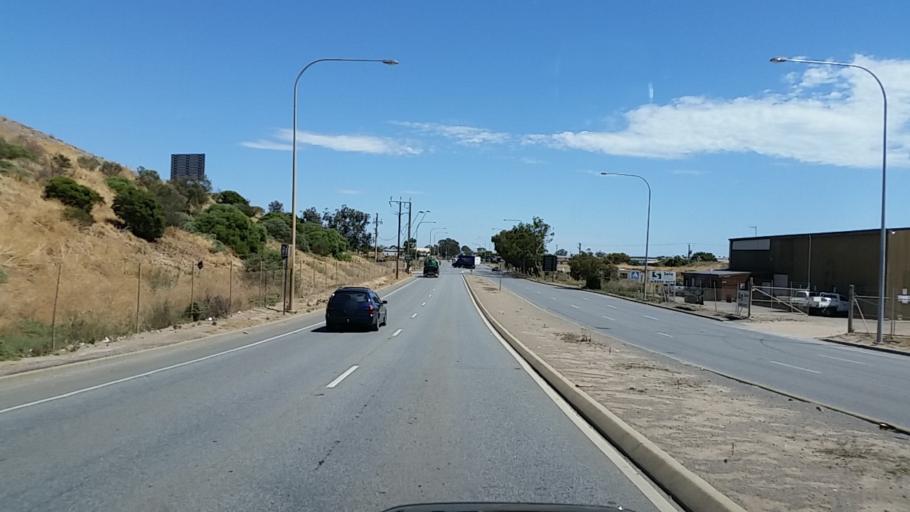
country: AU
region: South Australia
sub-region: Port Adelaide Enfield
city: Alberton
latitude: -34.8353
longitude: 138.5457
